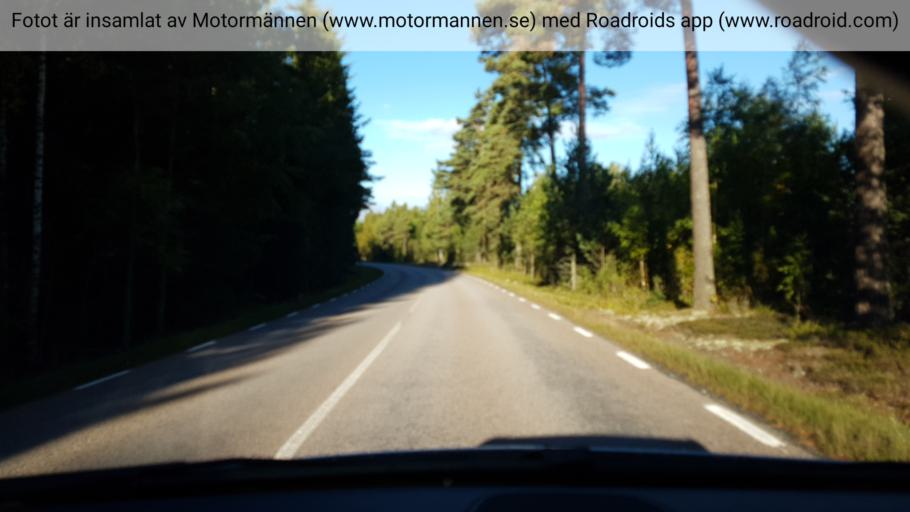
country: SE
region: Vaestra Goetaland
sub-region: Gotene Kommun
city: Goetene
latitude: 58.5449
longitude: 13.6762
